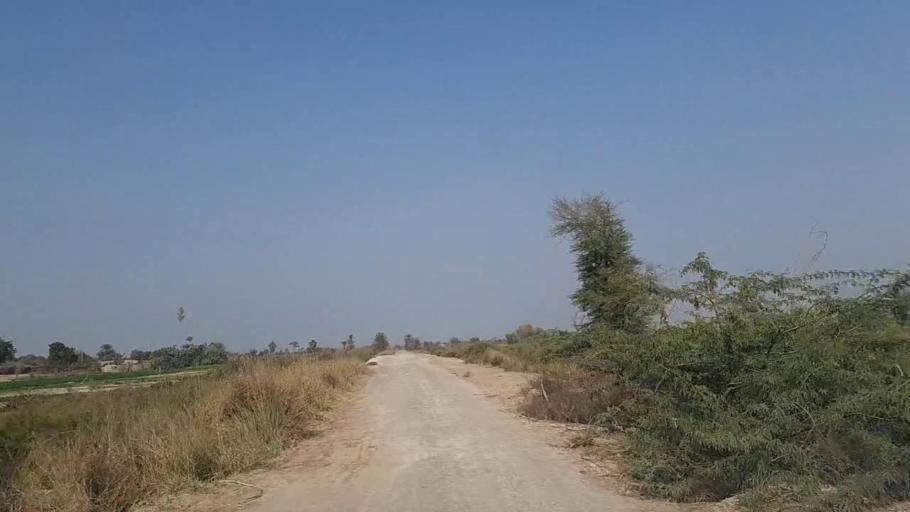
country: PK
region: Sindh
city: Daur
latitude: 26.4806
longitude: 68.4513
